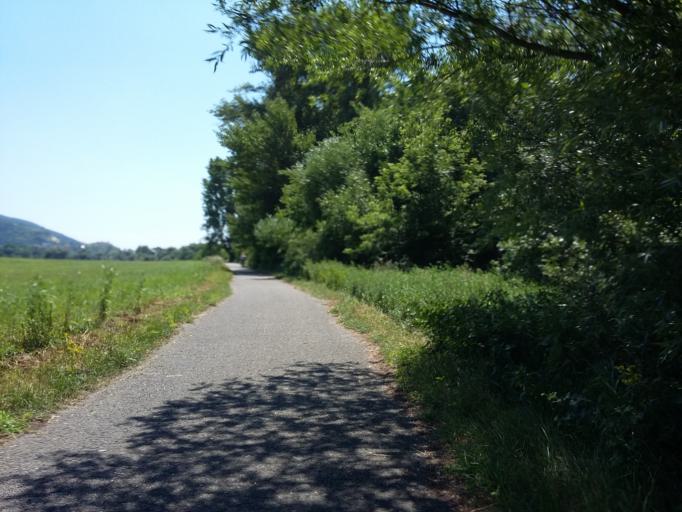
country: AT
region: Lower Austria
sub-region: Politischer Bezirk Bruck an der Leitha
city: Hainburg an der Donau
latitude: 48.2202
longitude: 16.9628
